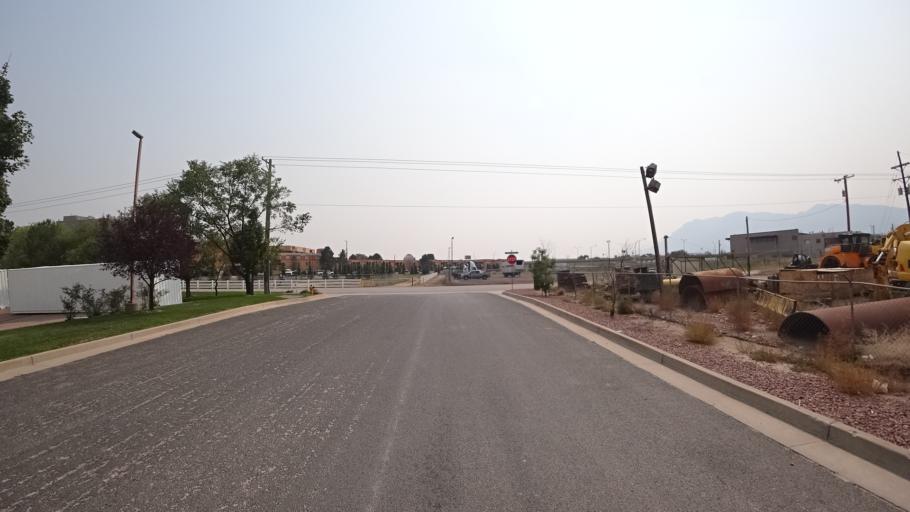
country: US
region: Colorado
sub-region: El Paso County
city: Stratmoor
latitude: 38.8000
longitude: -104.7969
